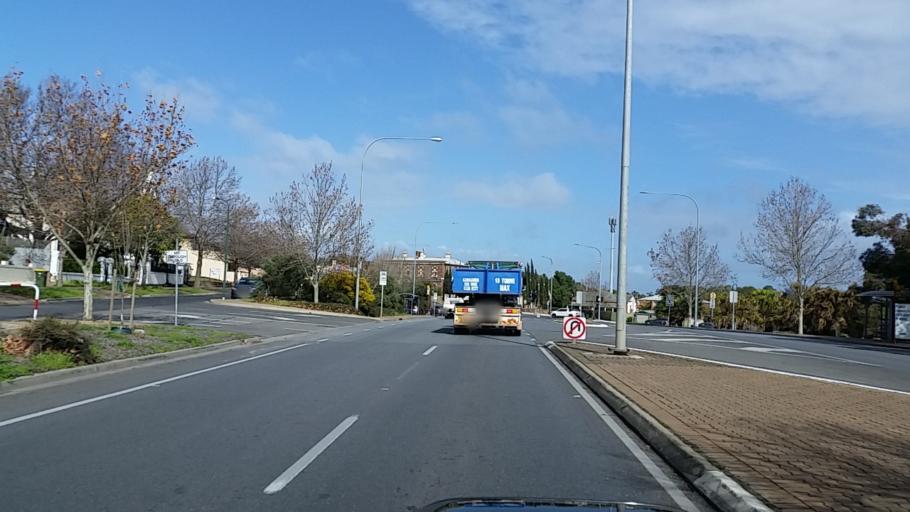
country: AU
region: South Australia
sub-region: Adelaide
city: North Adelaide
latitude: -34.8962
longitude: 138.5855
